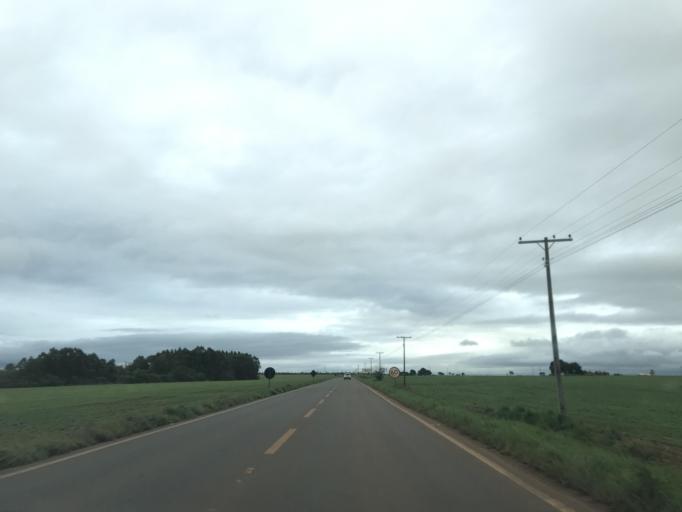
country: BR
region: Goias
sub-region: Luziania
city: Luziania
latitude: -16.3078
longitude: -48.0130
